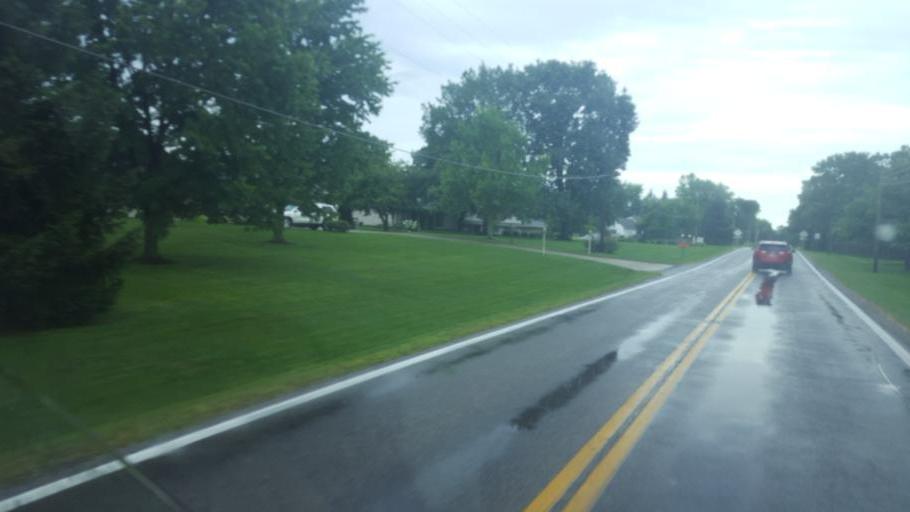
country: US
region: Ohio
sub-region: Marion County
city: Marion
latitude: 40.5638
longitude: -83.0848
